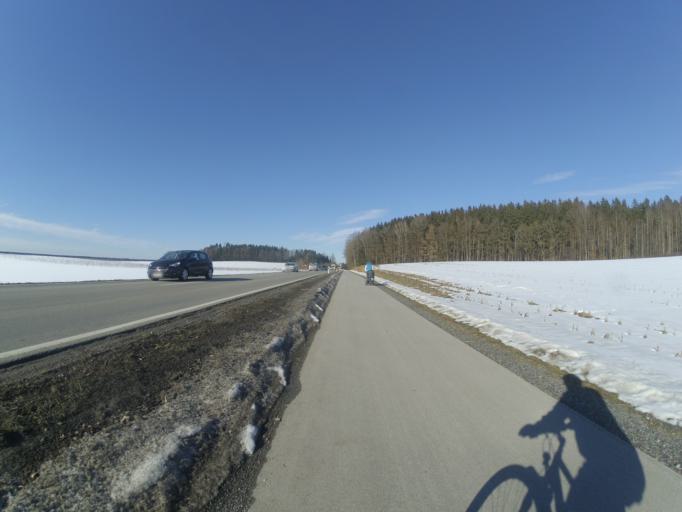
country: DE
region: Bavaria
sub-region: Upper Bavaria
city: Aying
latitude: 47.9539
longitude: 11.7852
